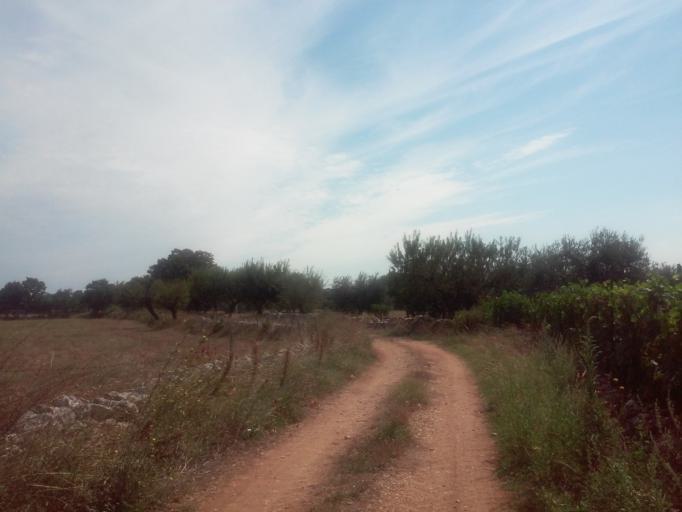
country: IT
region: Apulia
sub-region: Provincia di Bari
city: Gioia del Colle
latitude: 40.8198
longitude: 16.9599
